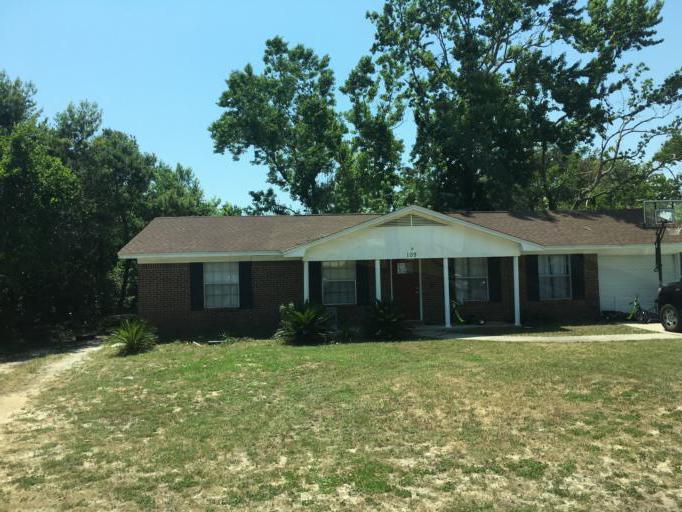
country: US
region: Florida
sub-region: Bay County
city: Laguna Beach
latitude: 30.2333
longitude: -85.8938
